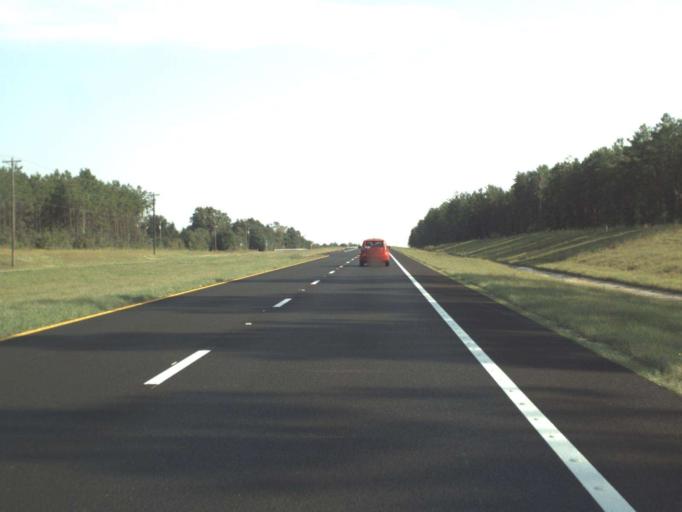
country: US
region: Florida
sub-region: Walton County
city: Freeport
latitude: 30.5318
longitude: -85.8368
